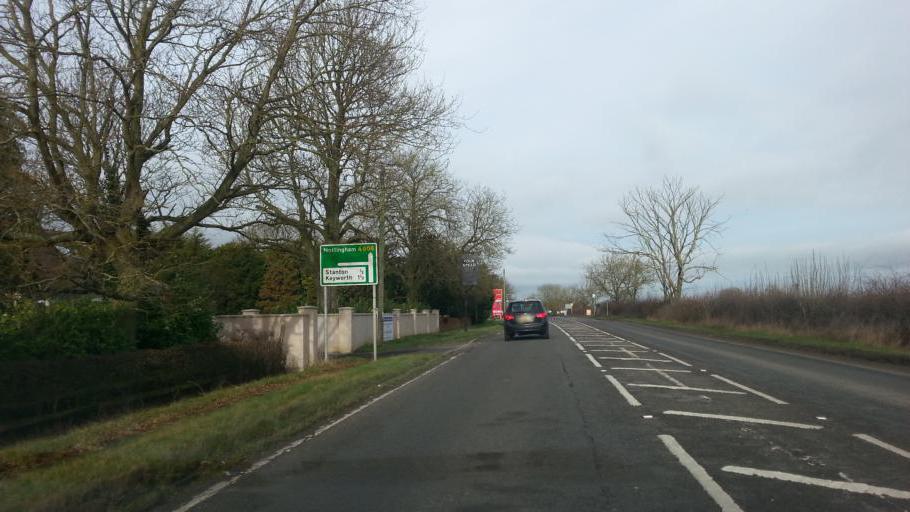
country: GB
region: England
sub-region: Nottinghamshire
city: Cotgrave
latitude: 52.8681
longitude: -1.0462
